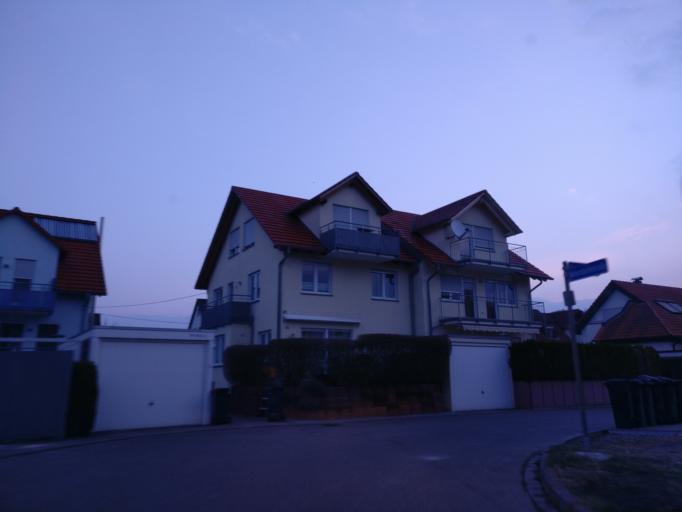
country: DE
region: Baden-Wuerttemberg
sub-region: Regierungsbezirk Stuttgart
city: Pluderhausen
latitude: 48.7916
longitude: 9.5971
